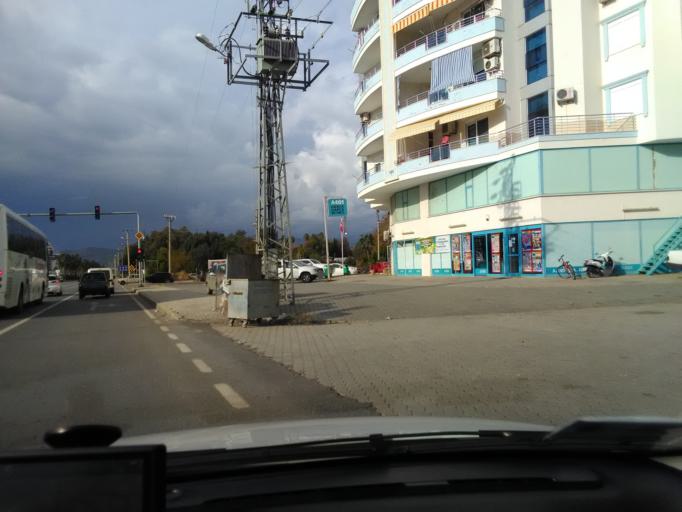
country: TR
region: Antalya
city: Gazipasa
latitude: 36.2629
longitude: 32.3201
